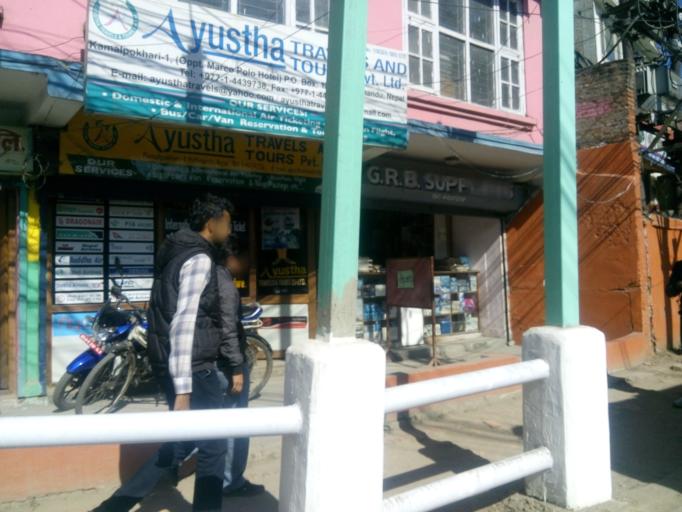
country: NP
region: Central Region
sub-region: Bagmati Zone
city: Kathmandu
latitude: 27.7107
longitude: 85.3220
